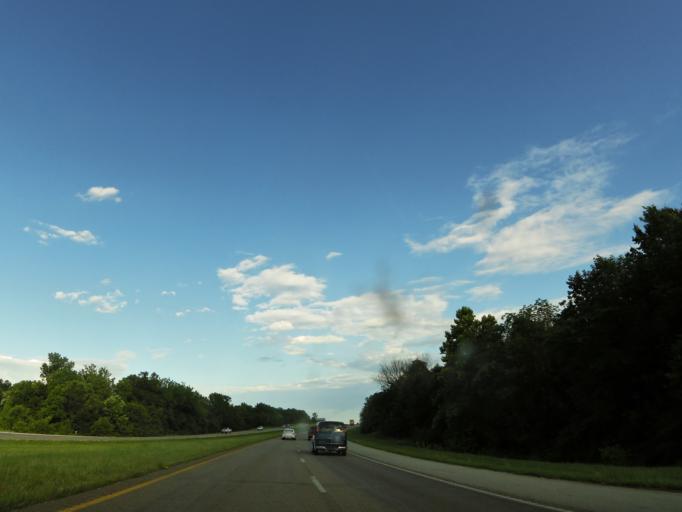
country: US
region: Missouri
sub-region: Saint Charles County
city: Wentzville
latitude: 38.8706
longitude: -90.8931
